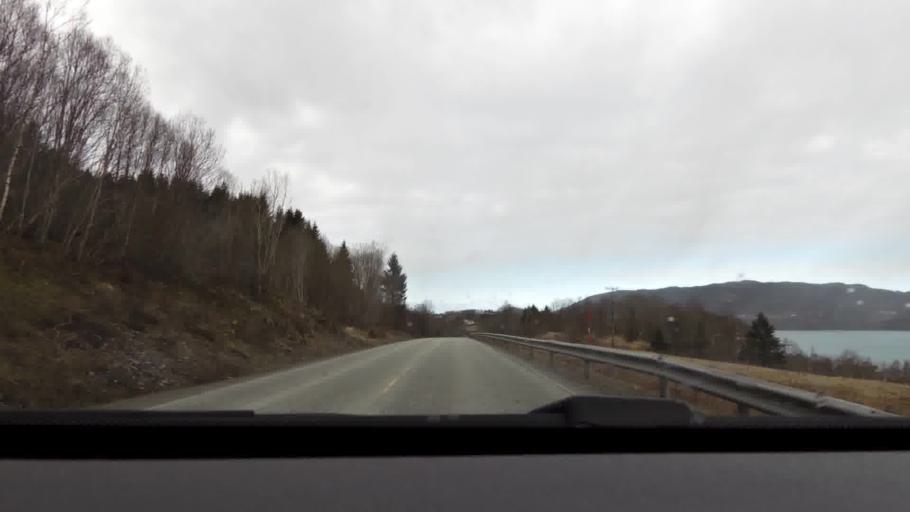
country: NO
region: More og Romsdal
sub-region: Kristiansund
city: Rensvik
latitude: 63.1092
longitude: 7.7849
